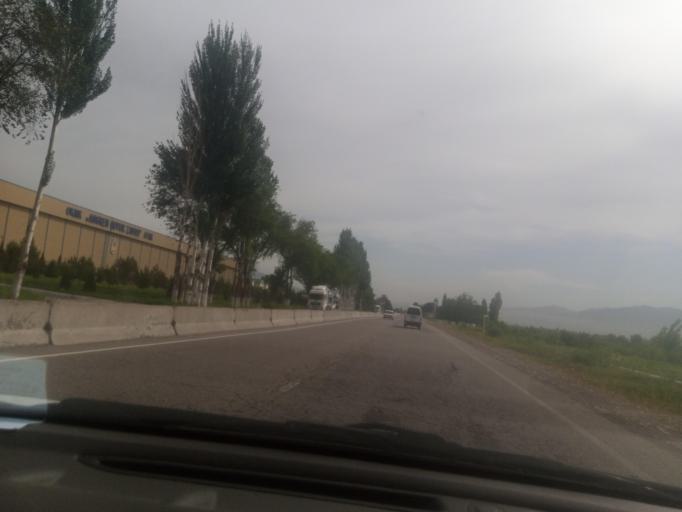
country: UZ
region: Toshkent
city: Angren
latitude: 40.9716
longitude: 69.9913
